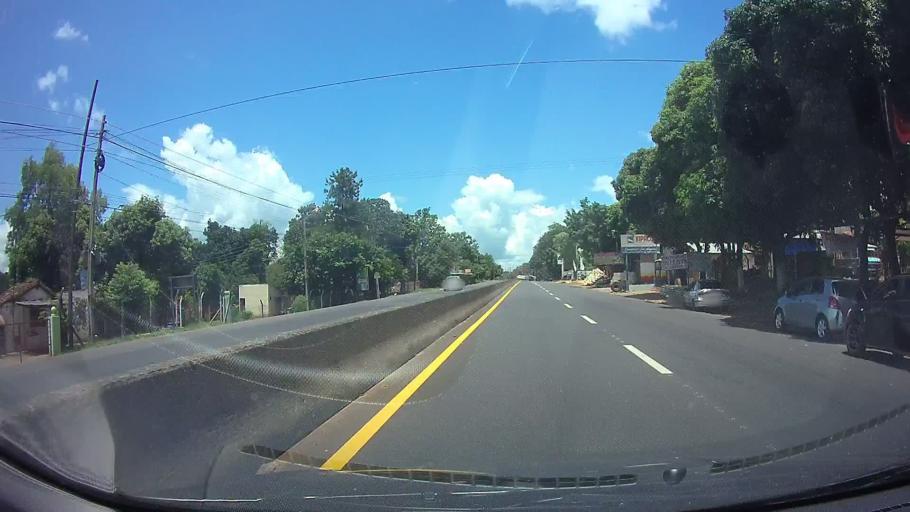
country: PY
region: Central
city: Itaugua
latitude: -25.3789
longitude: -57.3843
